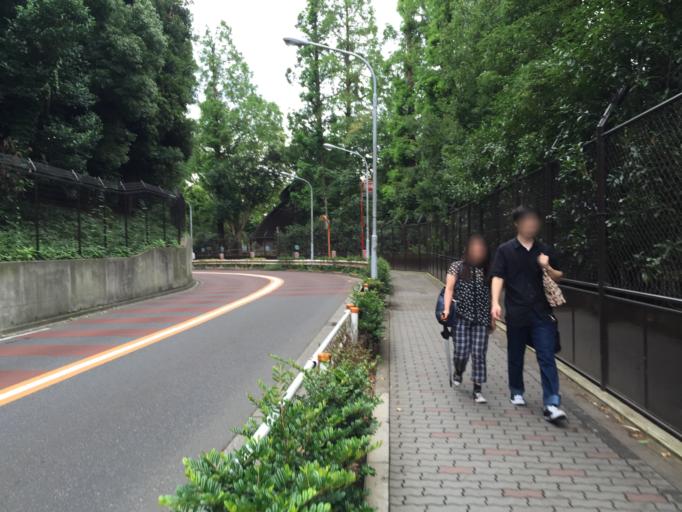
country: JP
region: Tokyo
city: Tokyo
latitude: 35.7151
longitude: 139.7699
